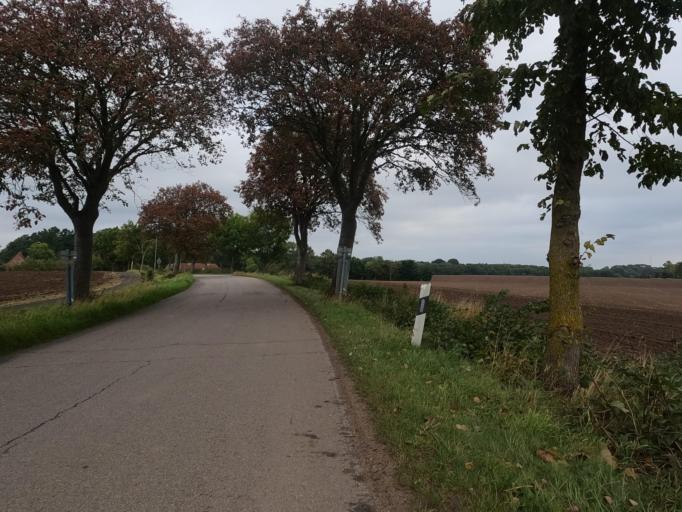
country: DE
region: Schleswig-Holstein
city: Neukirchen
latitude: 54.3272
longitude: 11.0316
